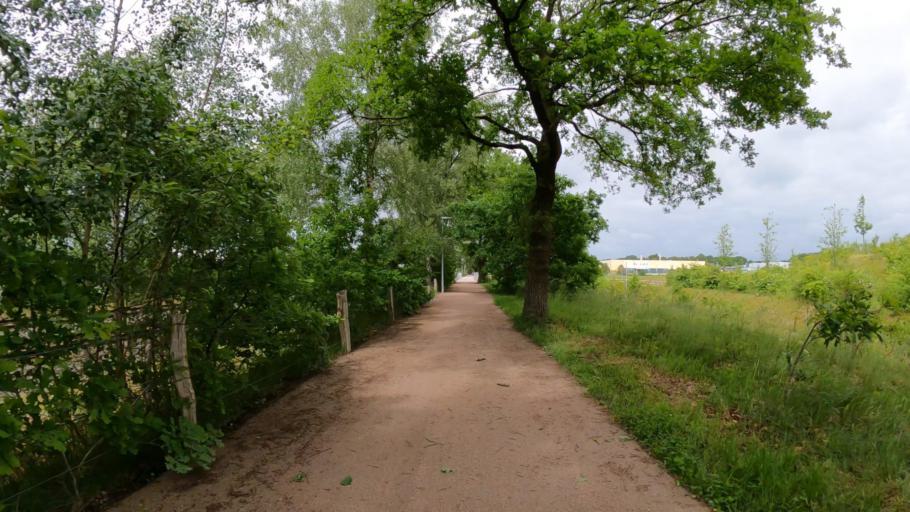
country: DE
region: Schleswig-Holstein
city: Norderstedt
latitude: 53.7212
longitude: 9.9912
